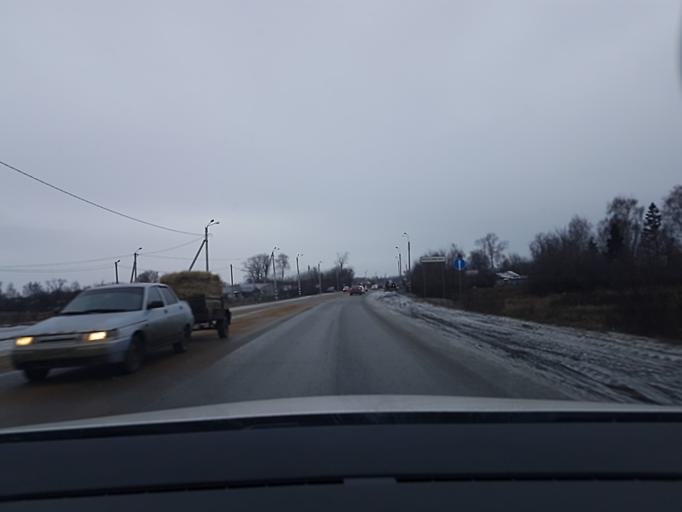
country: RU
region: Tambov
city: Zavoronezhskoye
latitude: 52.9619
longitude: 40.5727
